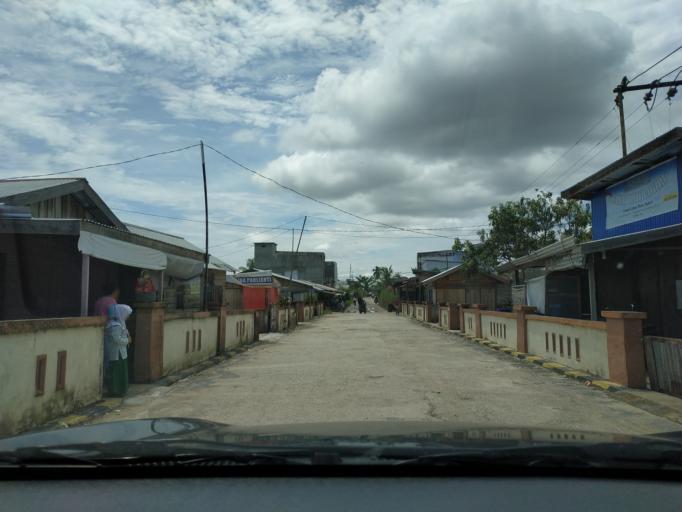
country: ID
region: Riau
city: Tembilahan
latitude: -0.3144
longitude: 103.1722
